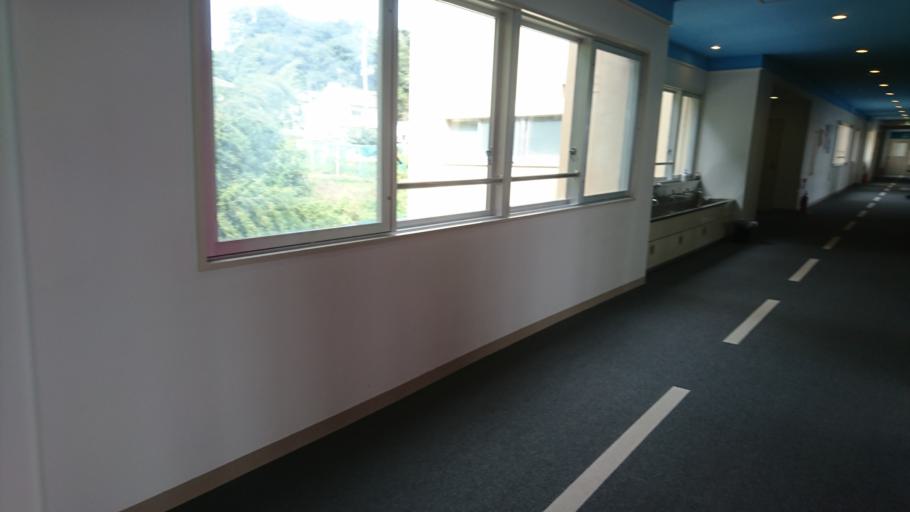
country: JP
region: Miyagi
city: Yamoto
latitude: 38.3758
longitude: 141.1532
